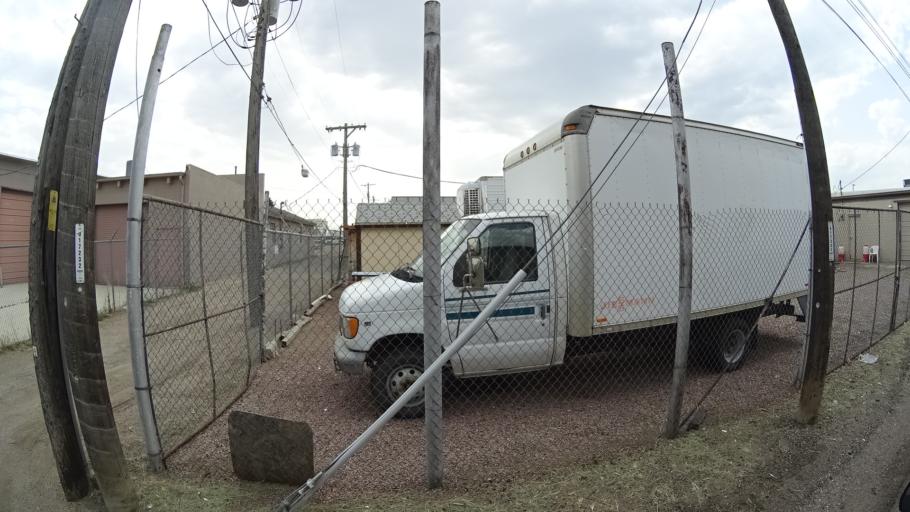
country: US
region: Colorado
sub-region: El Paso County
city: Colorado Springs
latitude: 38.8393
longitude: -104.7739
